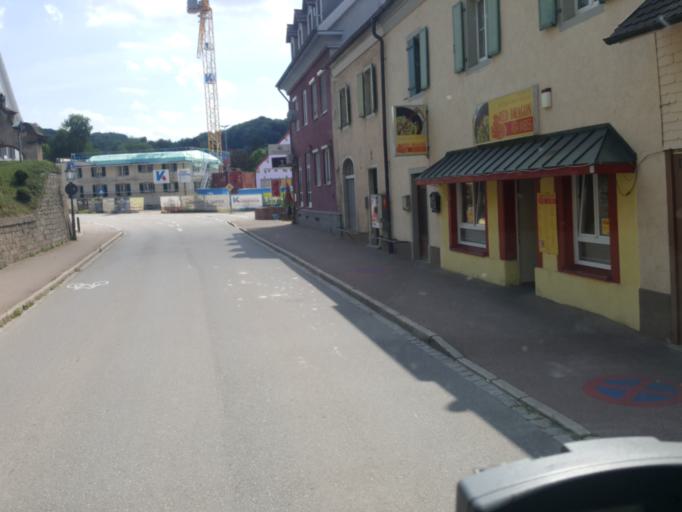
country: DE
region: Baden-Wuerttemberg
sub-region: Freiburg Region
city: Schliengen
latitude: 47.7565
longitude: 7.5771
